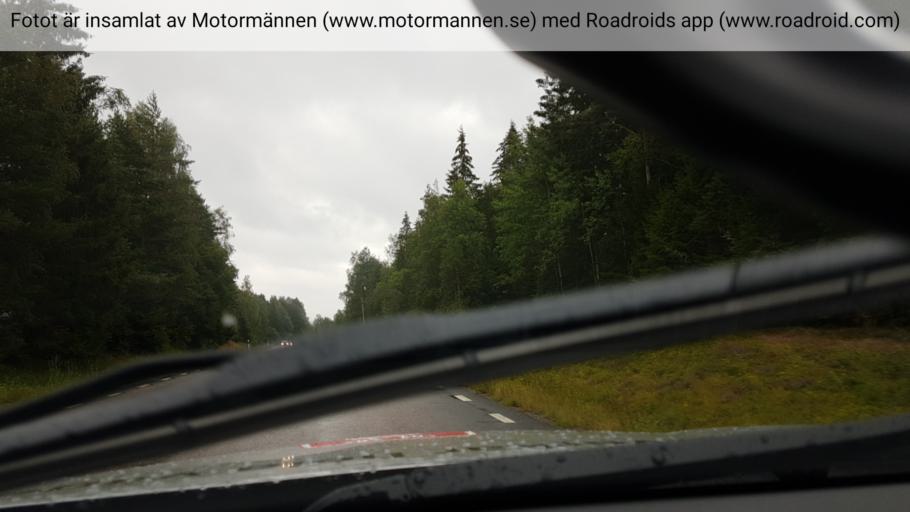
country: SE
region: Vaestra Goetaland
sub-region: Dals-Ed Kommun
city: Ed
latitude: 58.8775
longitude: 11.8779
